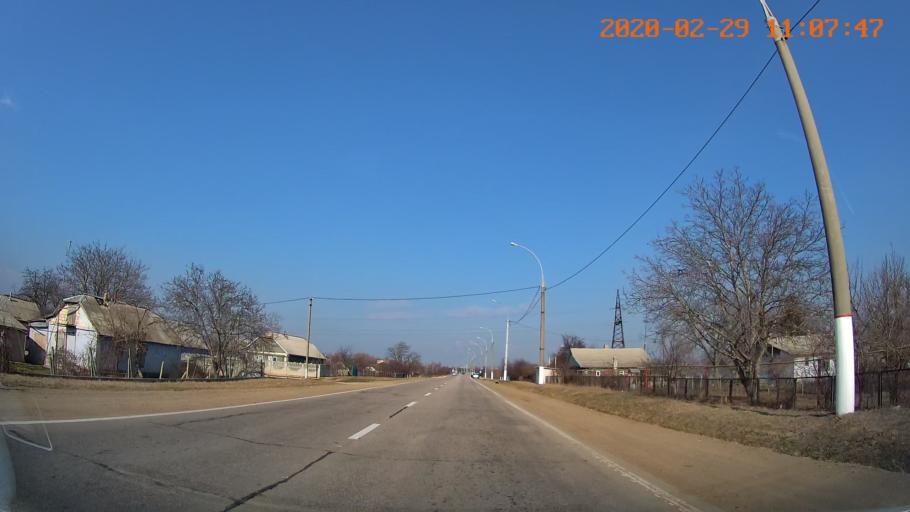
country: MD
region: Criuleni
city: Criuleni
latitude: 47.2282
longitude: 29.1799
